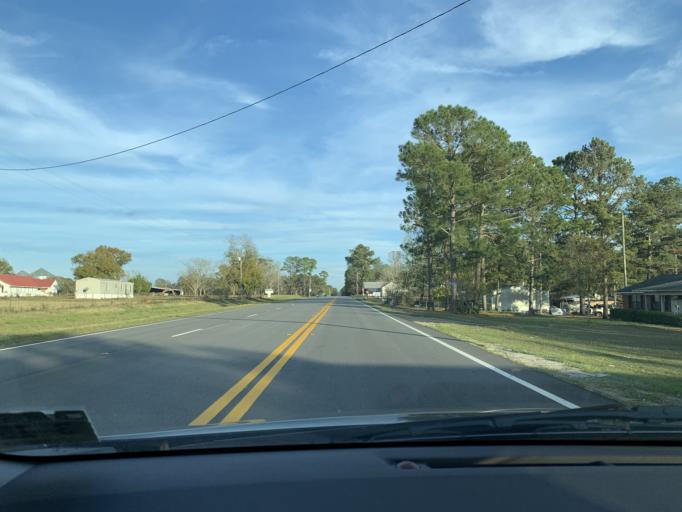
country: US
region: Georgia
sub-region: Irwin County
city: Ocilla
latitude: 31.5958
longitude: -83.1525
